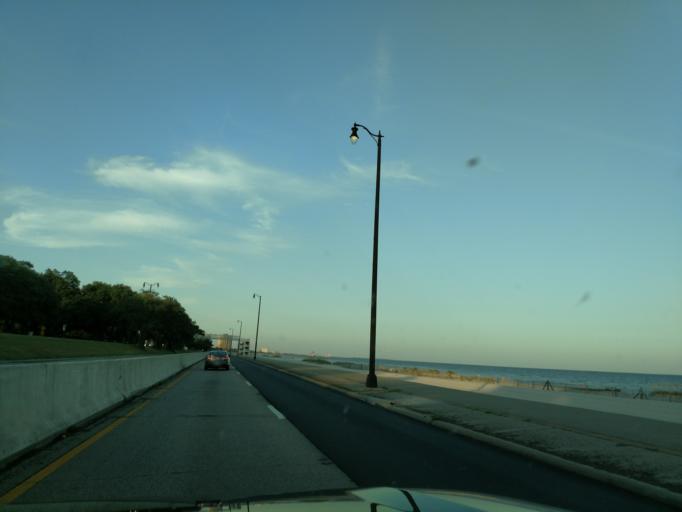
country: US
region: Mississippi
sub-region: Harrison County
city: Gulfport
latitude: 30.3840
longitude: -89.0198
